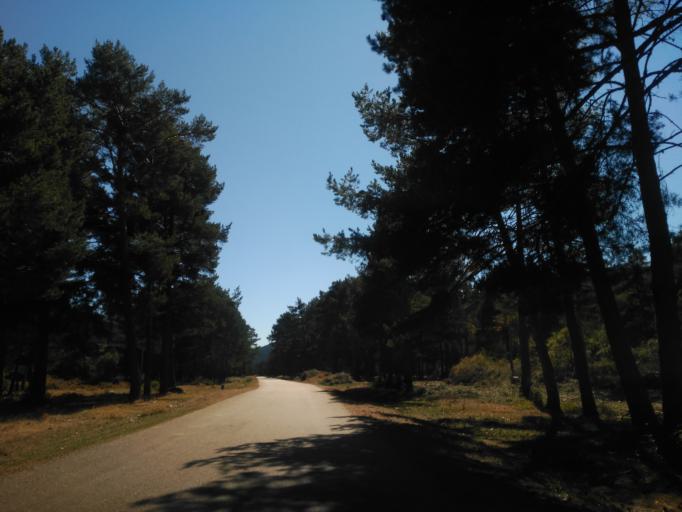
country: ES
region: Castille and Leon
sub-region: Provincia de Soria
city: Vinuesa
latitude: 41.9521
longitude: -2.7815
